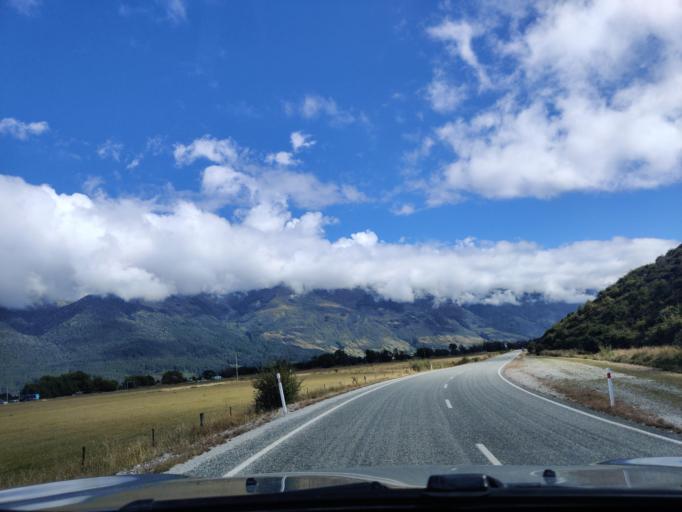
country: NZ
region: Otago
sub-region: Queenstown-Lakes District
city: Queenstown
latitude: -44.7994
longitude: 168.3717
